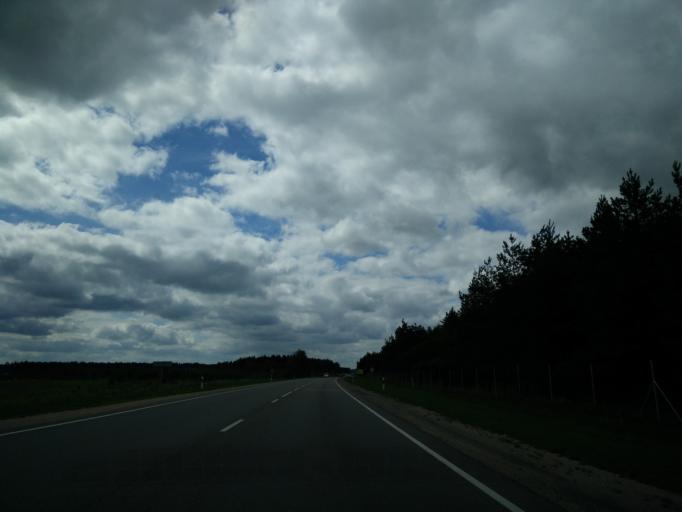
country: LT
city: Lentvaris
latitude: 54.6193
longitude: 25.0734
